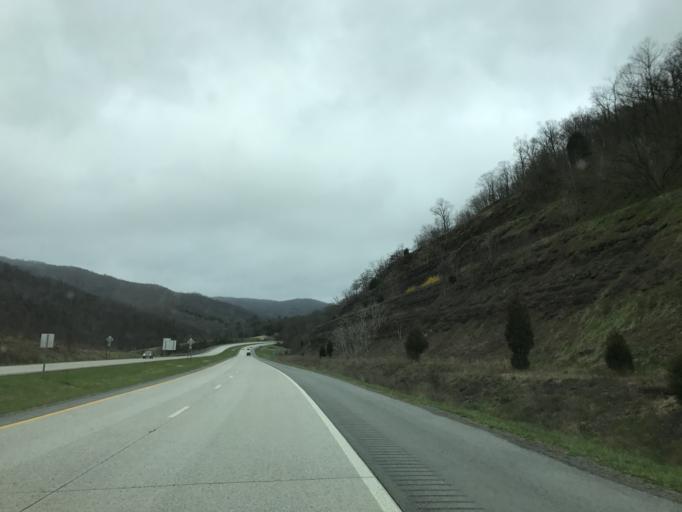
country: US
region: West Virginia
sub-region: Summers County
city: Hinton
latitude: 37.7868
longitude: -80.8780
